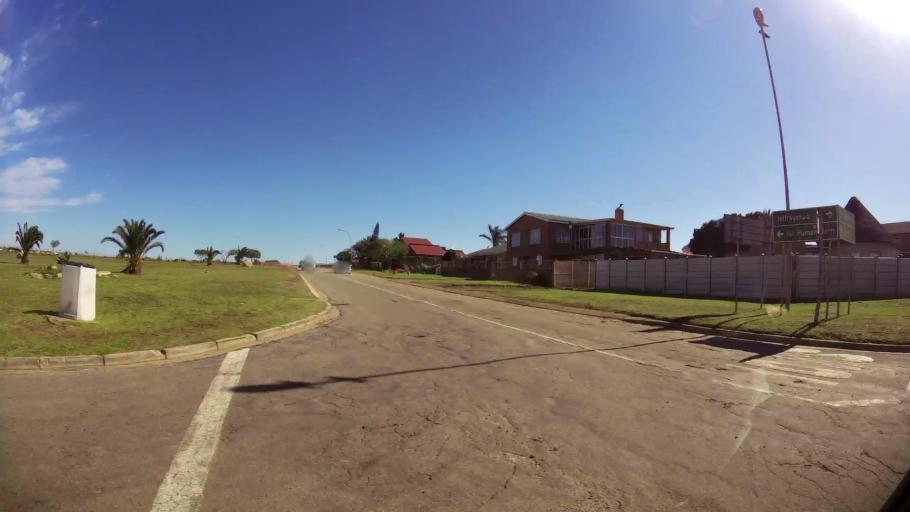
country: ZA
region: Eastern Cape
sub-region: Cacadu District Municipality
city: Jeffrey's Bay
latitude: -34.0544
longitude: 24.9151
